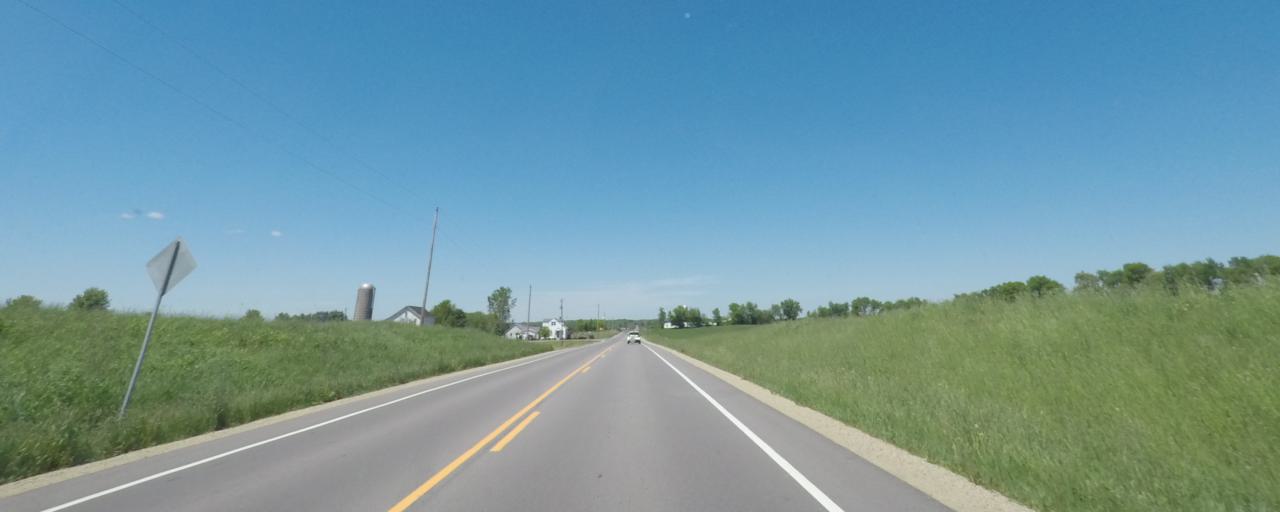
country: US
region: Wisconsin
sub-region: Green County
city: Brooklyn
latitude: 42.8262
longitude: -89.3693
